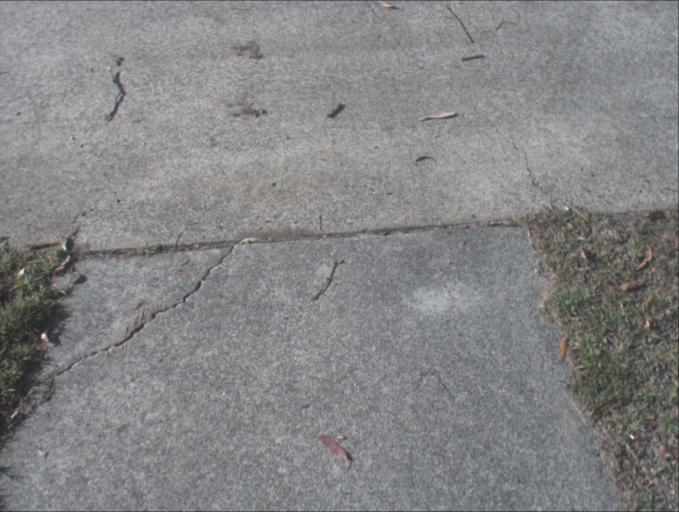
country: AU
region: Queensland
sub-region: Logan
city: Park Ridge South
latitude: -27.7011
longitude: 153.0267
